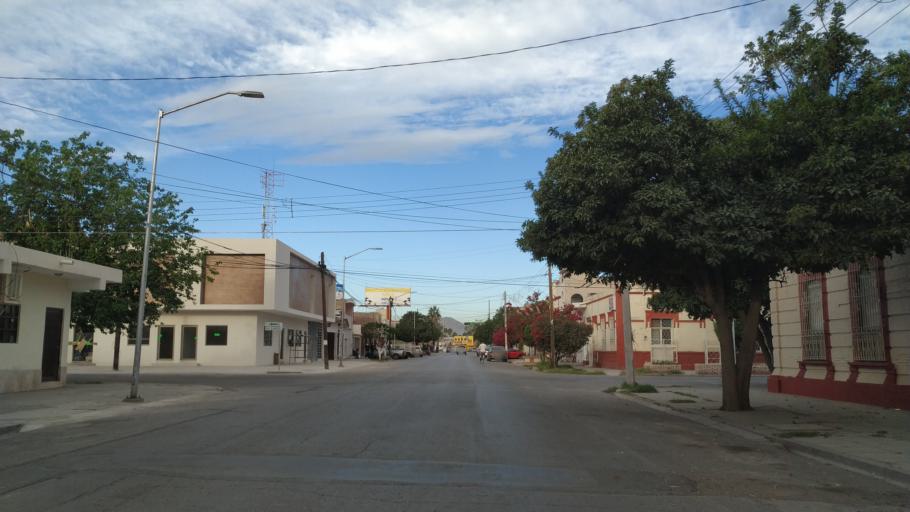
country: MX
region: Coahuila
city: Torreon
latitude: 25.5441
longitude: -103.4523
